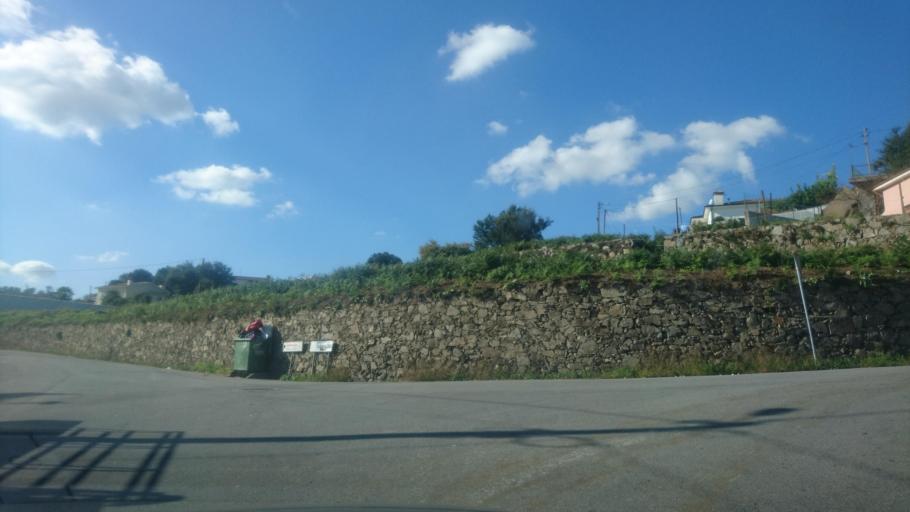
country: PT
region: Porto
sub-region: Paredes
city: Madalena
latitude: 41.2269
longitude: -8.3430
